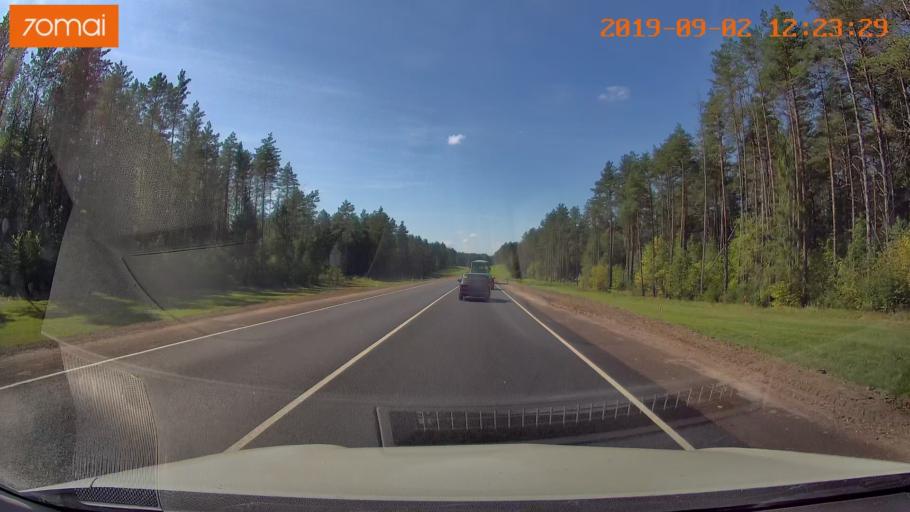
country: RU
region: Smolensk
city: Shumyachi
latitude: 53.8741
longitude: 32.6195
